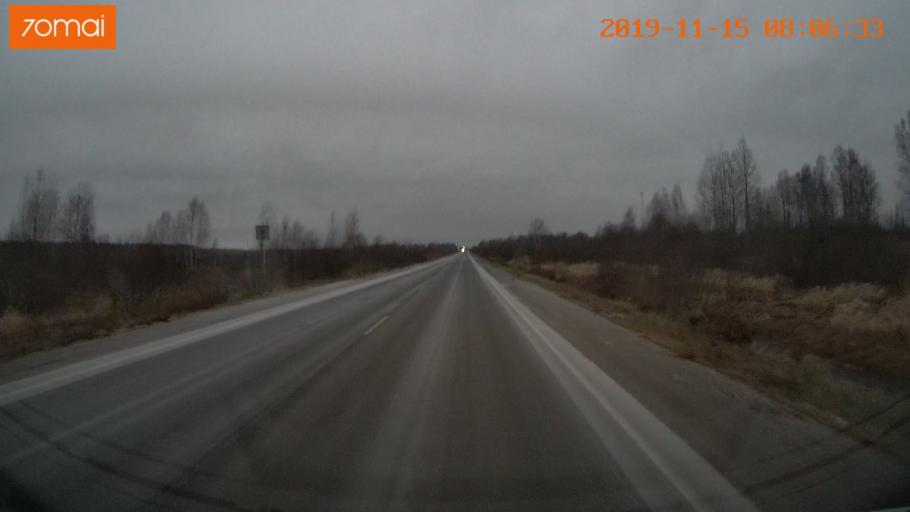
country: RU
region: Vologda
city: Cherepovets
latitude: 59.0226
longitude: 38.0362
